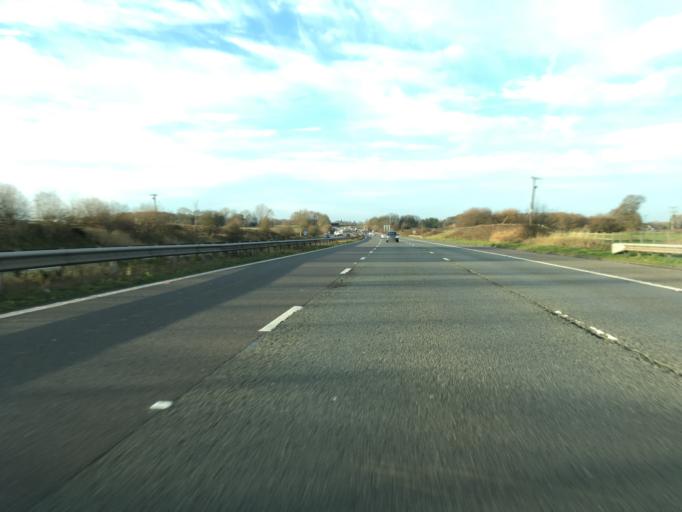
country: GB
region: England
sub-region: Trafford
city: Bowdon
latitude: 53.3637
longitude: -2.3924
